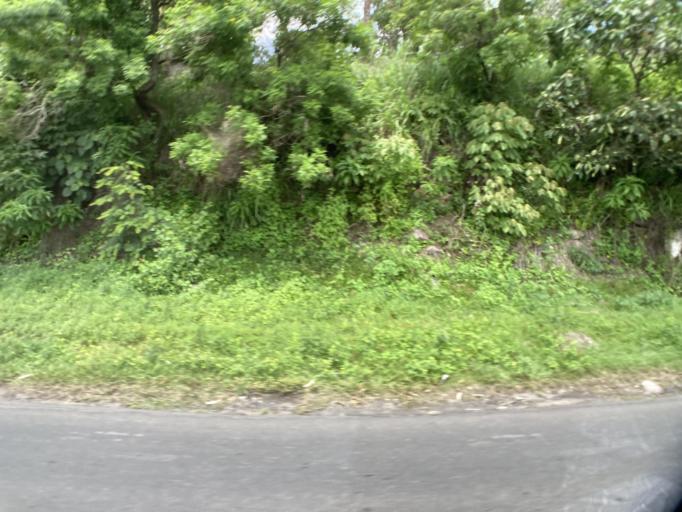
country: GT
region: Guatemala
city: Amatitlan
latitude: 14.4720
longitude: -90.5903
